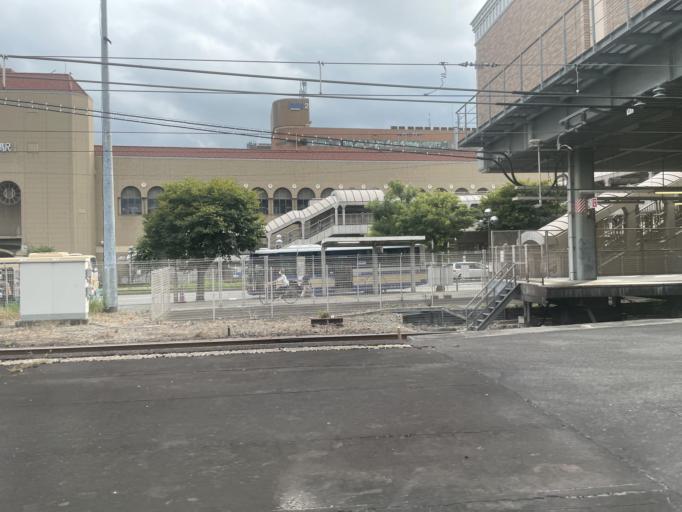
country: JP
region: Hyogo
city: Takarazuka
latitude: 34.8112
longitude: 135.3413
